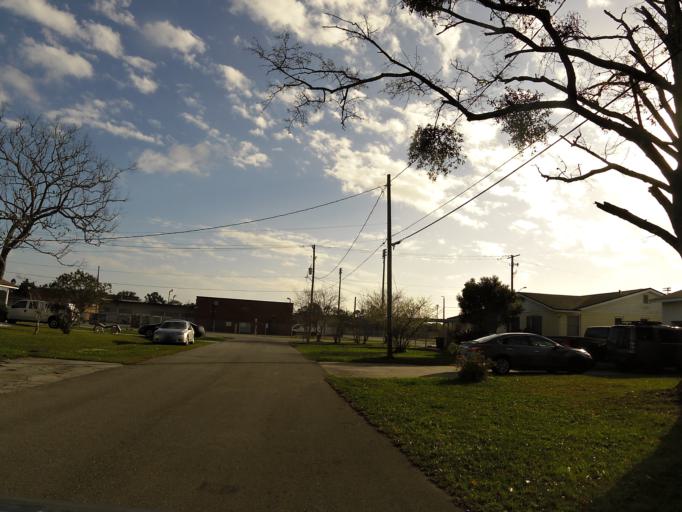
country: US
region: Florida
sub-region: Duval County
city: Jacksonville
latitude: 30.2796
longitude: -81.6127
